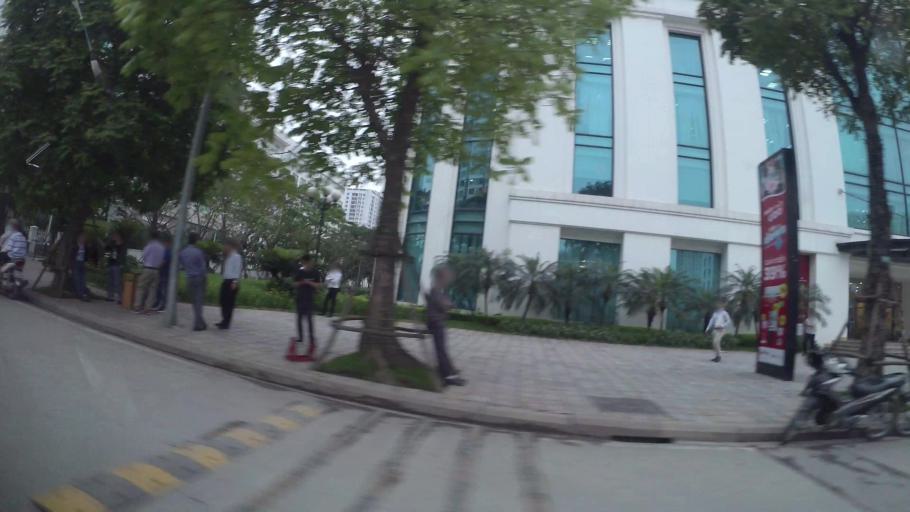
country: VN
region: Ha Noi
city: Hai BaTrung
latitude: 20.9971
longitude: 105.8675
